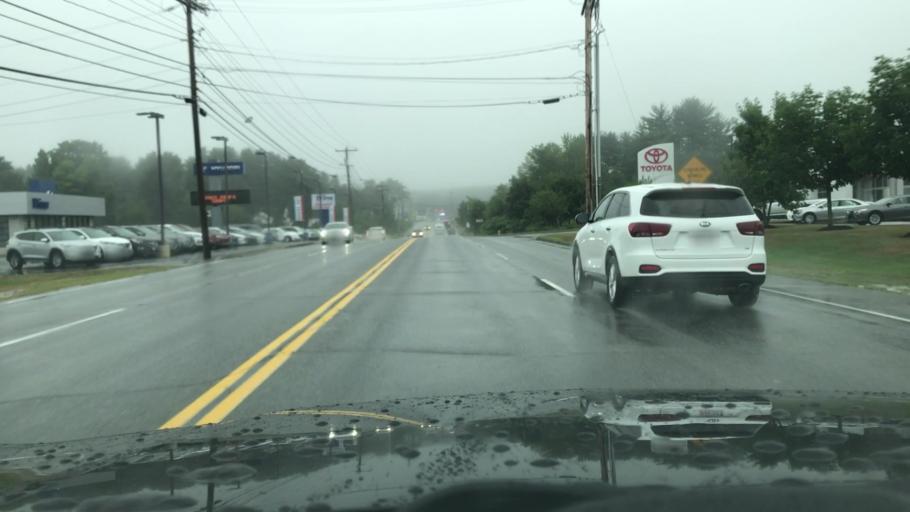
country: US
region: Maine
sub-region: York County
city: Saco
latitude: 43.5293
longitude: -70.4263
